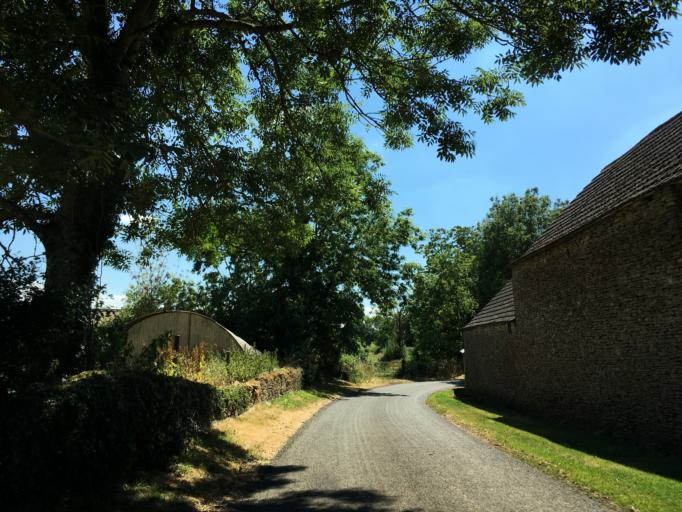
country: GB
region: England
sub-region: Wiltshire
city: Luckington
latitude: 51.5616
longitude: -2.2143
